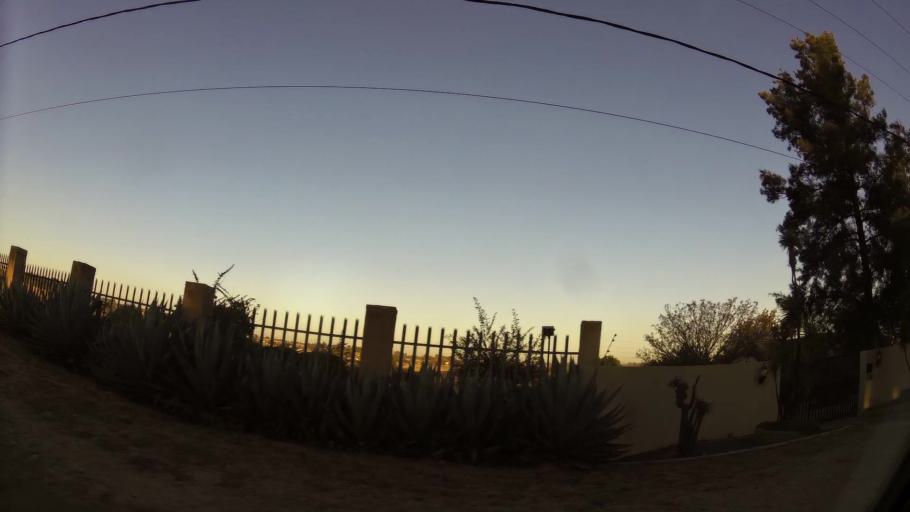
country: ZA
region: Gauteng
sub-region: City of Johannesburg Metropolitan Municipality
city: Diepsloot
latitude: -25.9420
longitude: 28.0540
